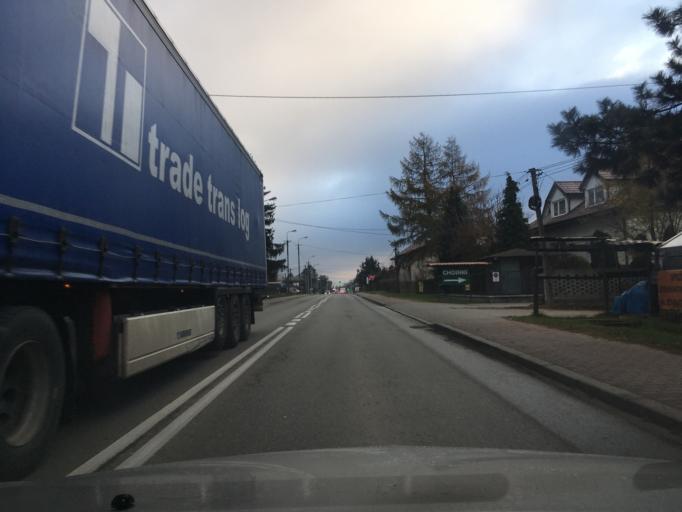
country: PL
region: Masovian Voivodeship
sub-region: Powiat piaseczynski
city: Lesznowola
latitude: 52.0870
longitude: 20.9439
